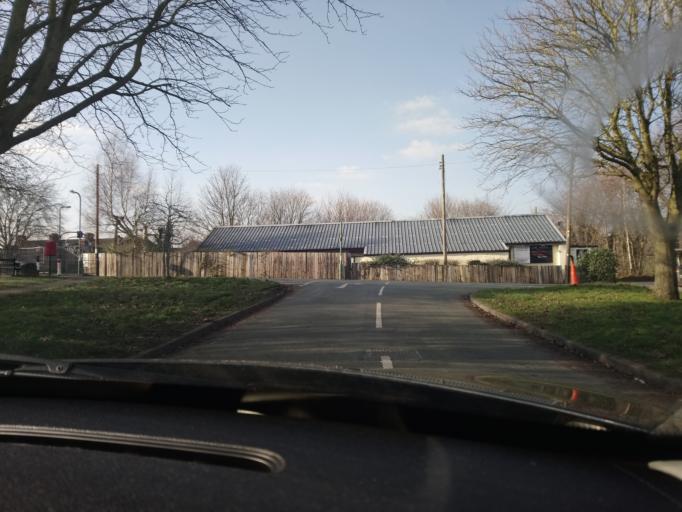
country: GB
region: England
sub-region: Shropshire
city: Shrewsbury
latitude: 52.7011
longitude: -2.7417
